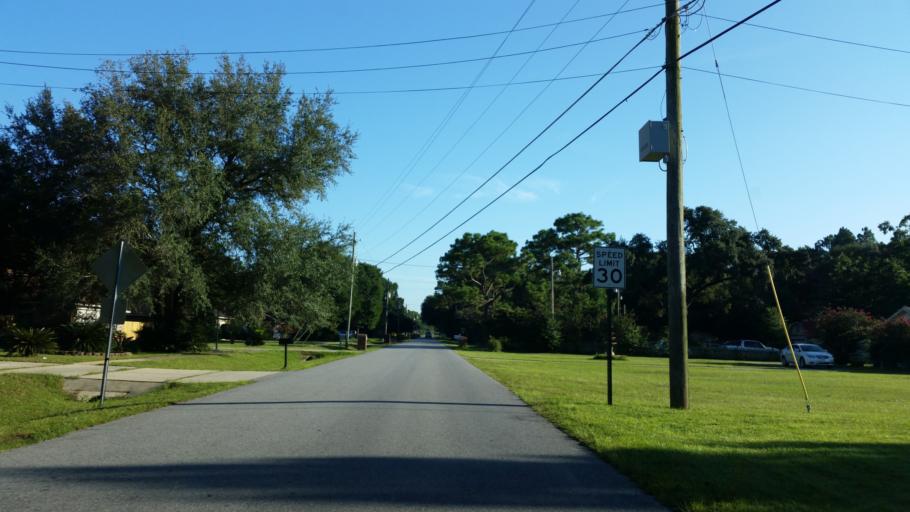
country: US
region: Florida
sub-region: Escambia County
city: Bellview
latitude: 30.4988
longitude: -87.3567
